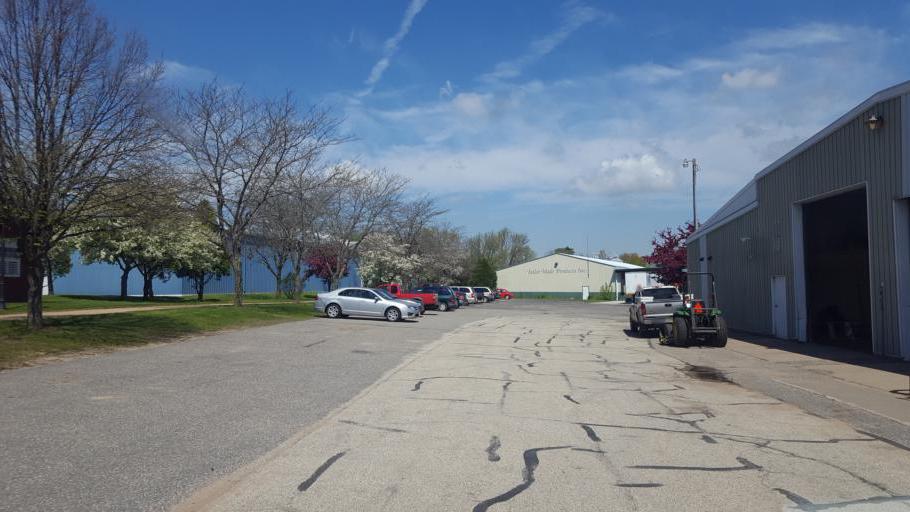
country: US
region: Wisconsin
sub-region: Juneau County
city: Elroy
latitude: 43.7401
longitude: -90.2702
